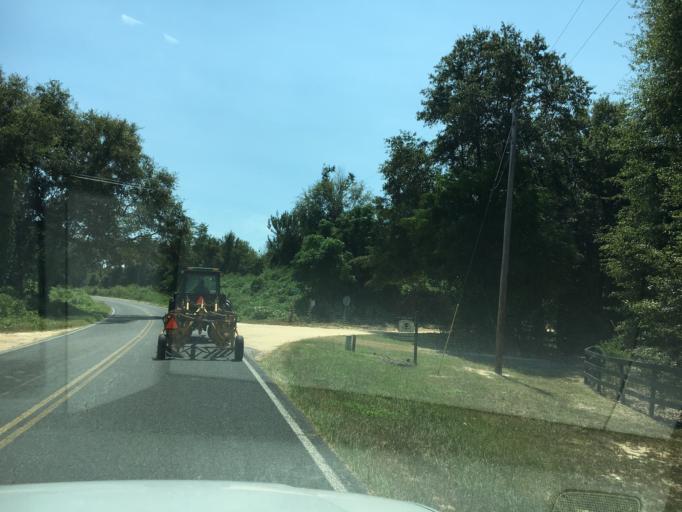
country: US
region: South Carolina
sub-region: Lexington County
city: Batesburg
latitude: 33.8028
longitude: -81.6461
